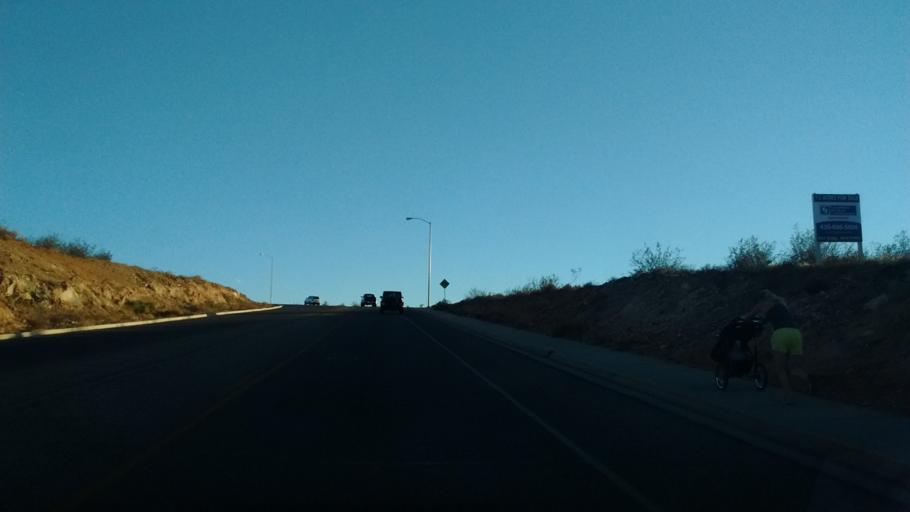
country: US
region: Utah
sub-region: Washington County
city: Saint George
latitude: 37.0946
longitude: -113.5504
